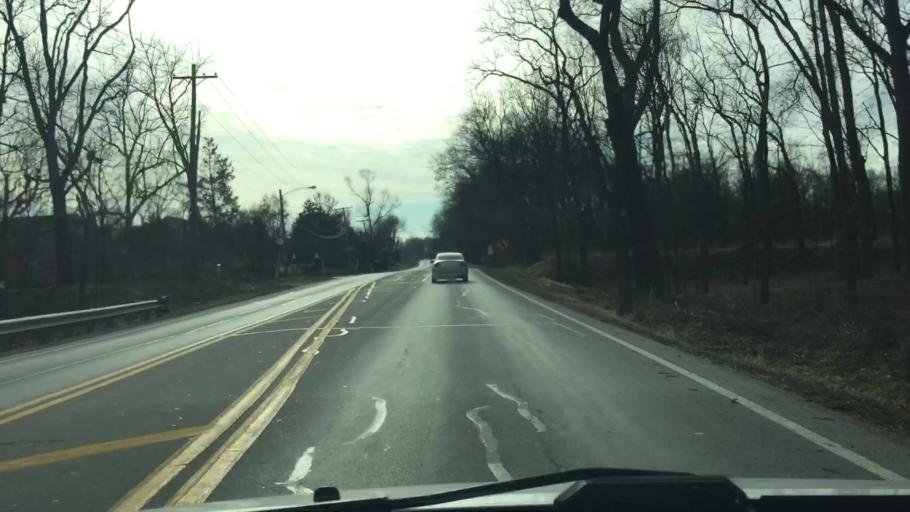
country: US
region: Illinois
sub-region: DuPage County
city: Wayne
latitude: 41.9481
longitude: -88.2719
